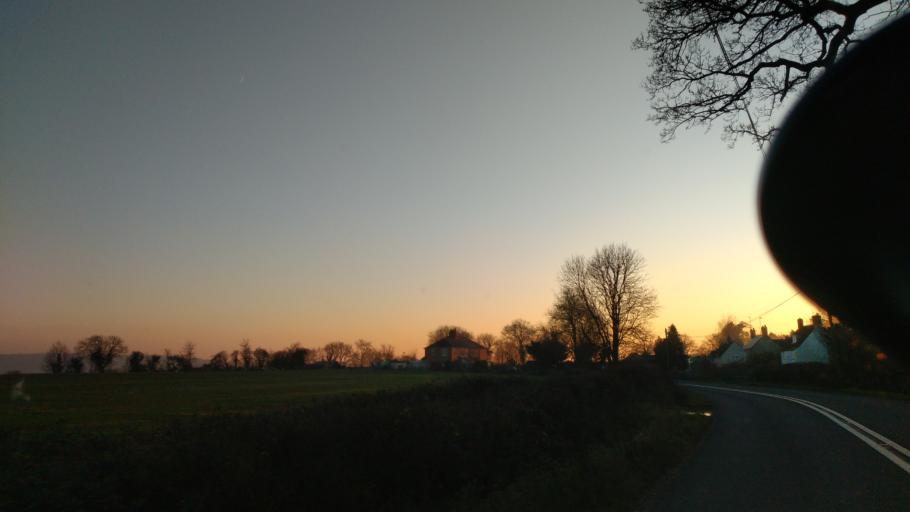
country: GB
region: England
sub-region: Wiltshire
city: Calne
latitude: 51.4204
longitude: -2.0126
